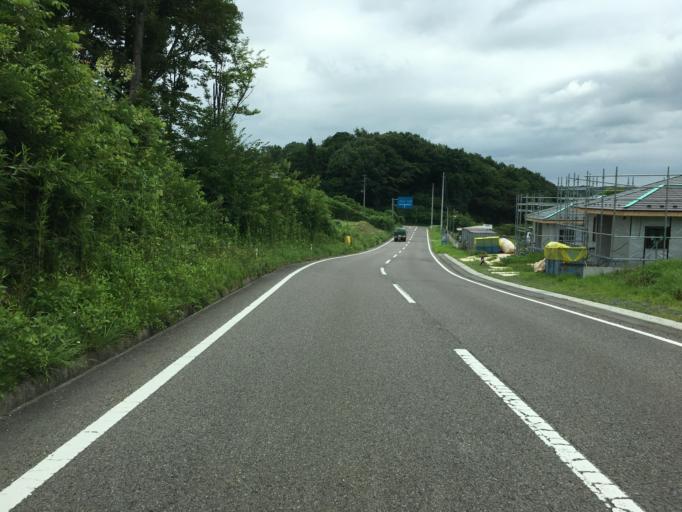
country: JP
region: Fukushima
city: Nihommatsu
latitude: 37.5748
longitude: 140.4295
